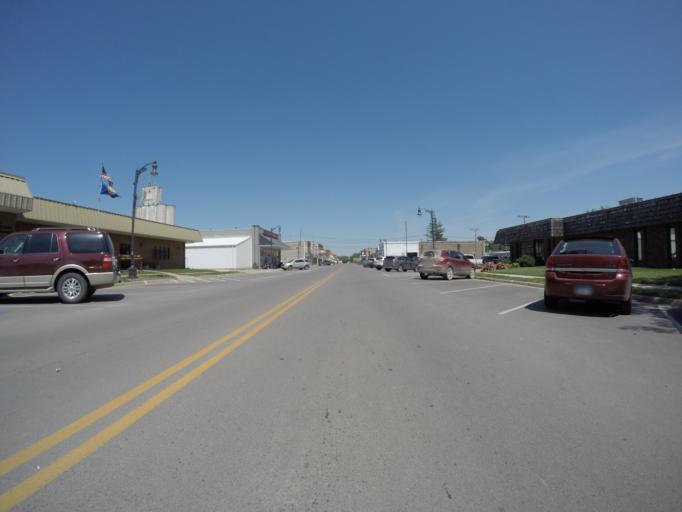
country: US
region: Kansas
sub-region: Nemaha County
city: Sabetha
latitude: 39.9034
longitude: -95.8046
